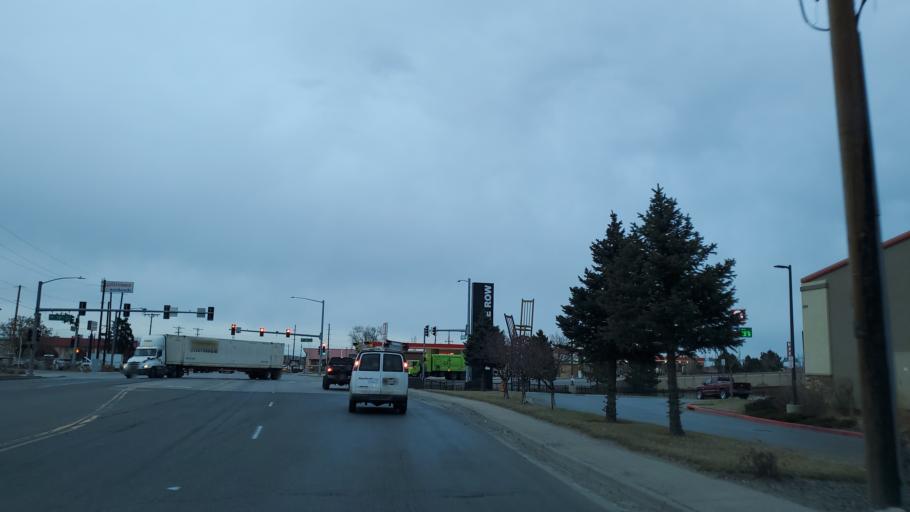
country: US
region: Colorado
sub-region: Adams County
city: Twin Lakes
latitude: 39.8010
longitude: -104.9873
